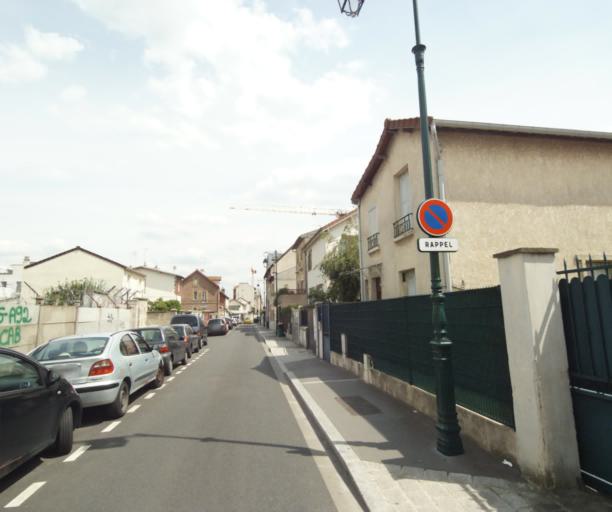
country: FR
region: Ile-de-France
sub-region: Departement des Hauts-de-Seine
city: Colombes
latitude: 48.9150
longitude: 2.2513
